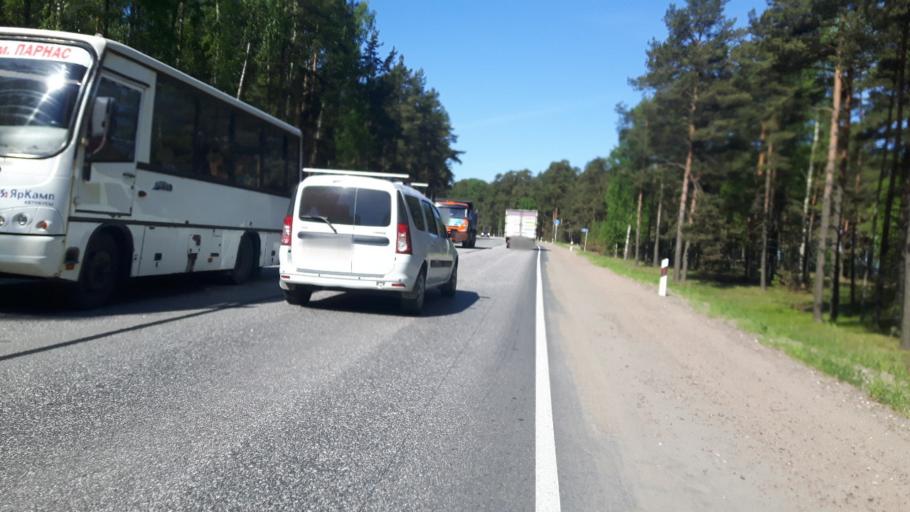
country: RU
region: Leningrad
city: Lebyazh'ye
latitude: 59.9567
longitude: 29.4674
